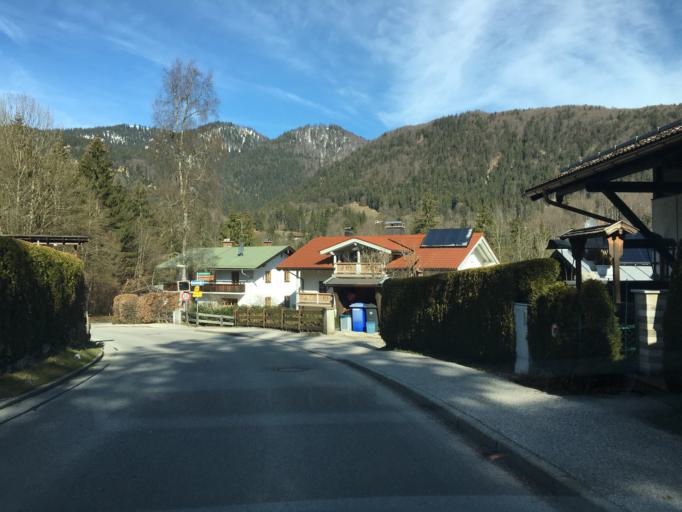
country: DE
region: Bavaria
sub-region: Upper Bavaria
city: Schoenau am Koenigssee
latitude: 47.6121
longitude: 12.9583
